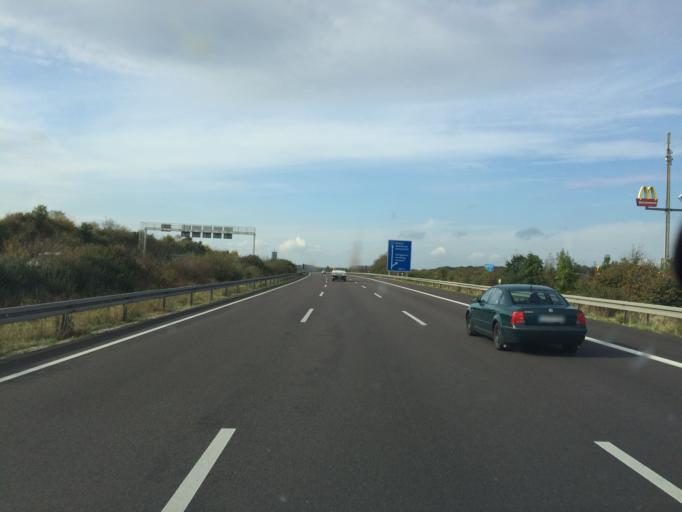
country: DE
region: Lower Saxony
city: Konigslutter am Elm
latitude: 52.3101
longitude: 10.8273
